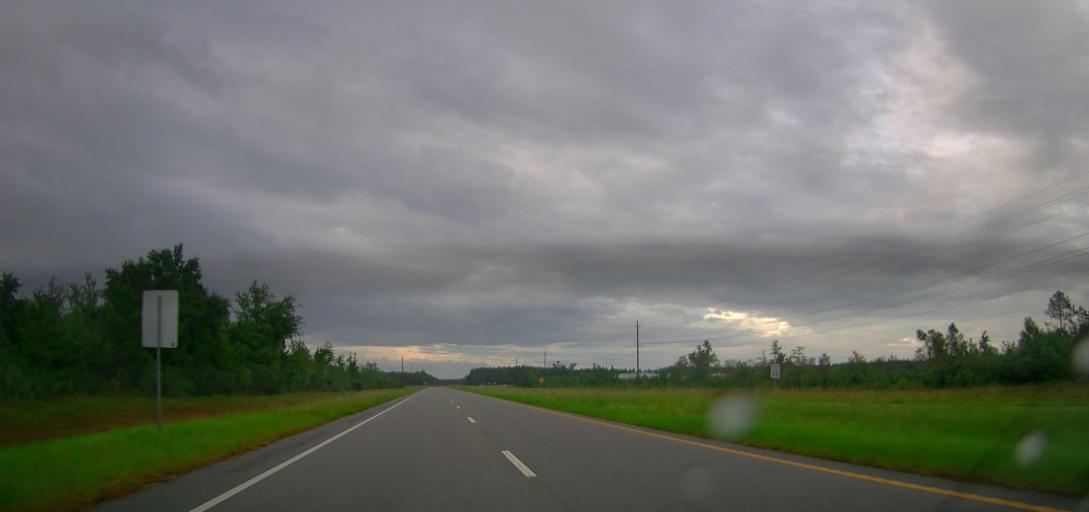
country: US
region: Georgia
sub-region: Ware County
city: Deenwood
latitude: 31.2541
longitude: -82.4299
